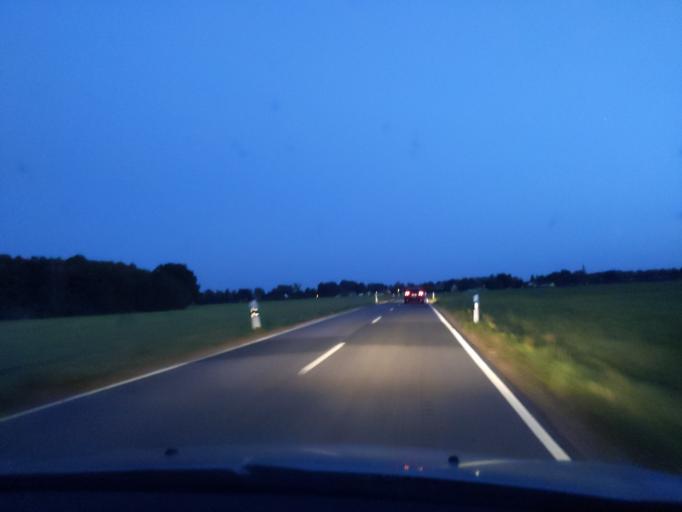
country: DE
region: Saxony
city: Malschwitz
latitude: 51.2725
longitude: 14.5207
